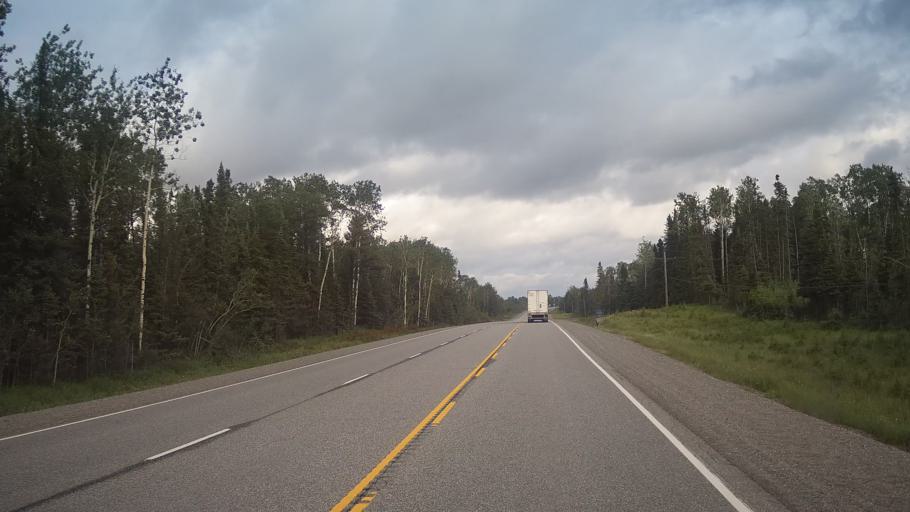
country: CA
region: Ontario
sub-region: Rainy River District
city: Atikokan
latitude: 49.0014
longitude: -90.4047
